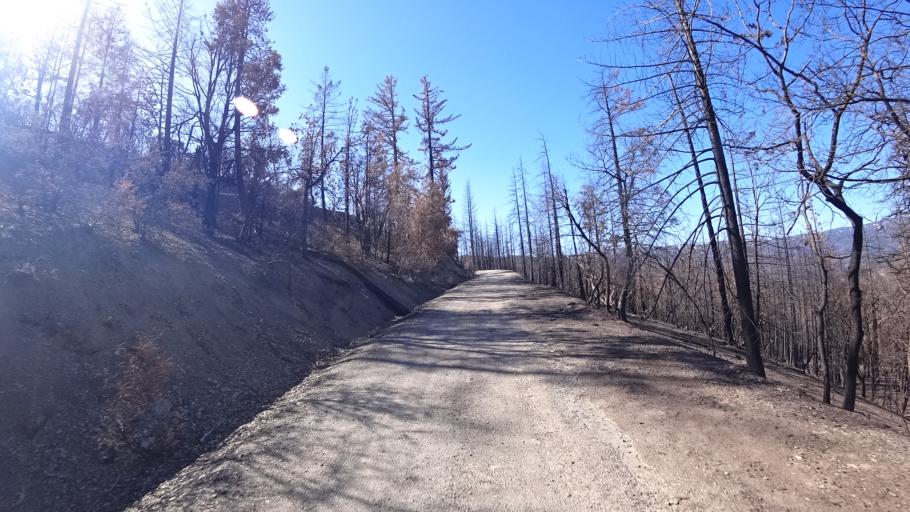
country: US
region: California
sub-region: Tehama County
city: Rancho Tehama Reserve
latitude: 39.6766
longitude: -122.7089
